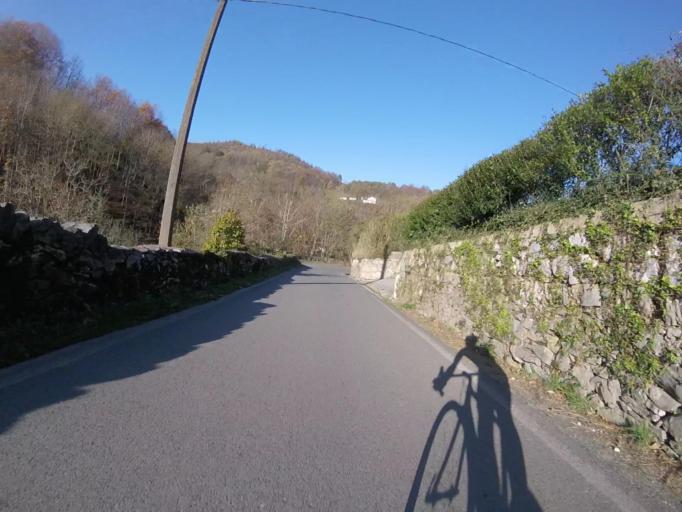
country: ES
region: Navarre
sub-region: Provincia de Navarra
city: Igantzi
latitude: 43.2363
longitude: -1.7028
